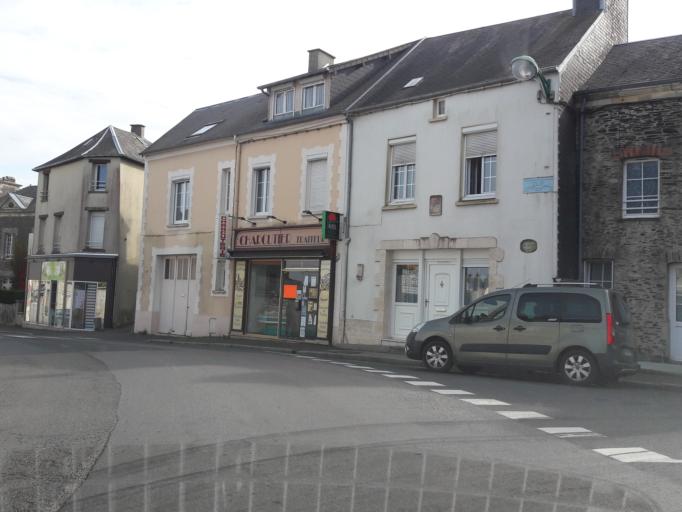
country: FR
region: Lower Normandy
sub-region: Departement du Calvados
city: Cahagnes
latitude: 49.0906
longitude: -0.8043
